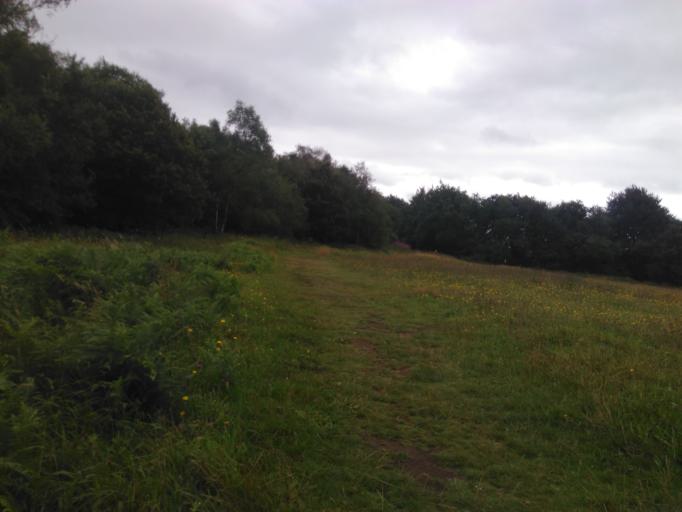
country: GB
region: England
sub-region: Devon
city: Uffculme
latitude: 50.9481
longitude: -3.2290
